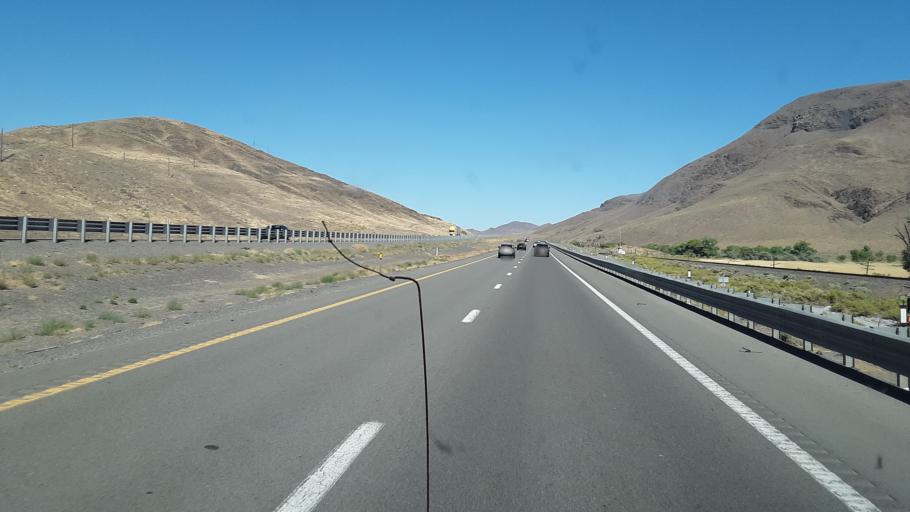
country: US
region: Nevada
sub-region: Lyon County
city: Fernley
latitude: 39.5915
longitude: -119.4486
